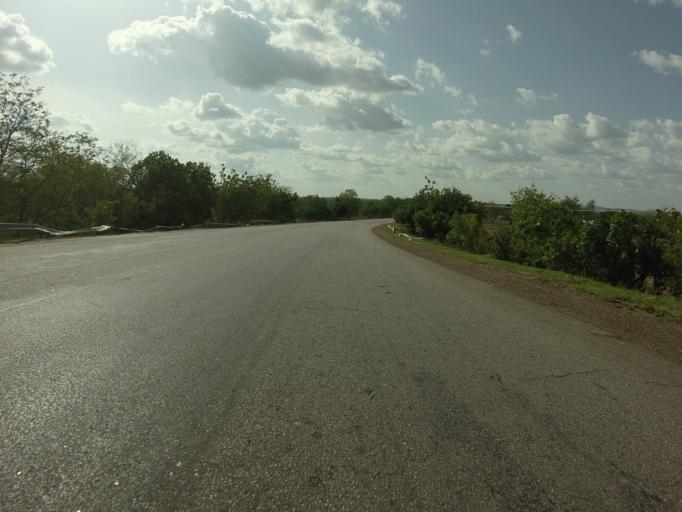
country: GH
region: Upper East
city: Bolgatanga
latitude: 10.5572
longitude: -0.8322
